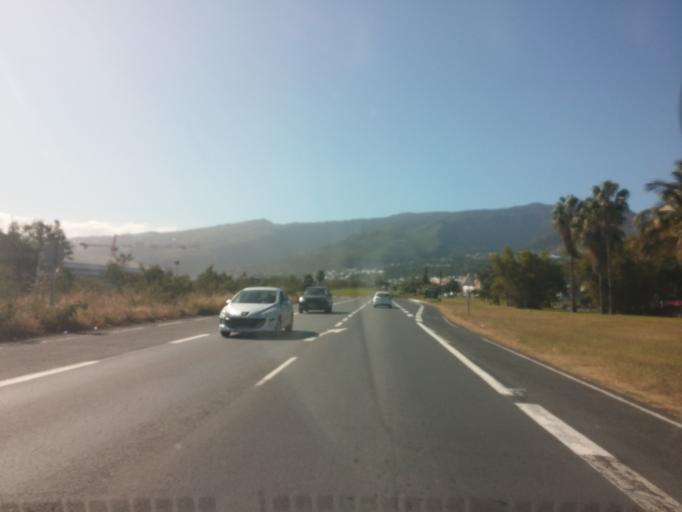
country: RE
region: Reunion
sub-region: Reunion
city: Le Port
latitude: -20.9449
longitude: 55.3155
